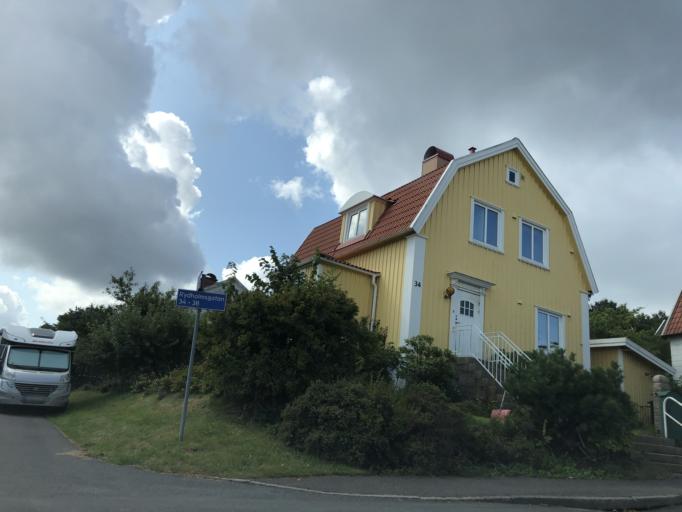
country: SE
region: Vaestra Goetaland
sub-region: Goteborg
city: Majorna
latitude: 57.7116
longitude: 11.8994
